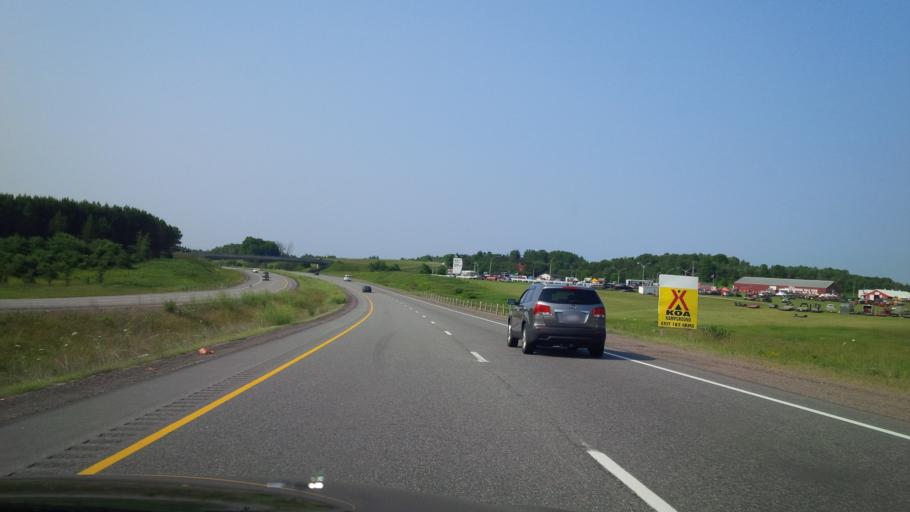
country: CA
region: Ontario
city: Bracebridge
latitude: 45.0390
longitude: -79.2909
